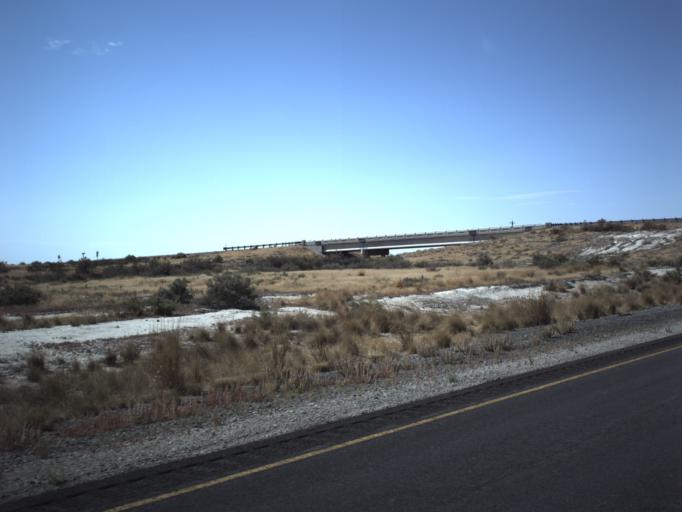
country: US
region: Utah
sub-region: Tooele County
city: Grantsville
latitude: 40.7327
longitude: -113.1127
